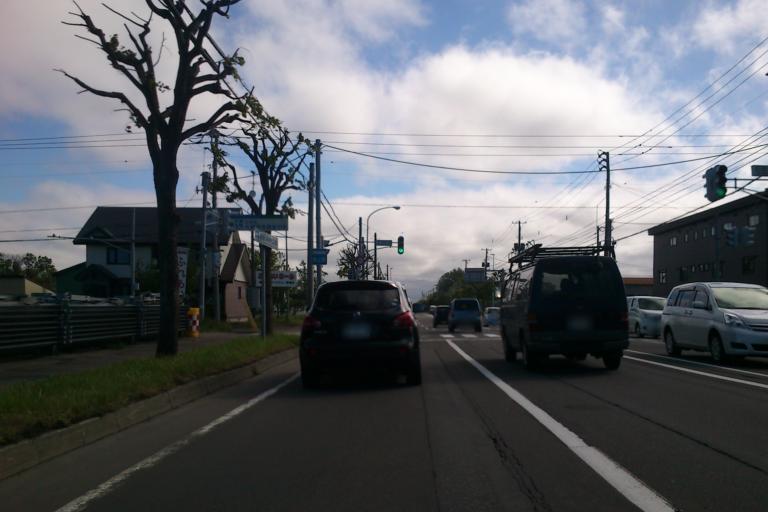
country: JP
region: Hokkaido
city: Sapporo
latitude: 43.1367
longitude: 141.2679
